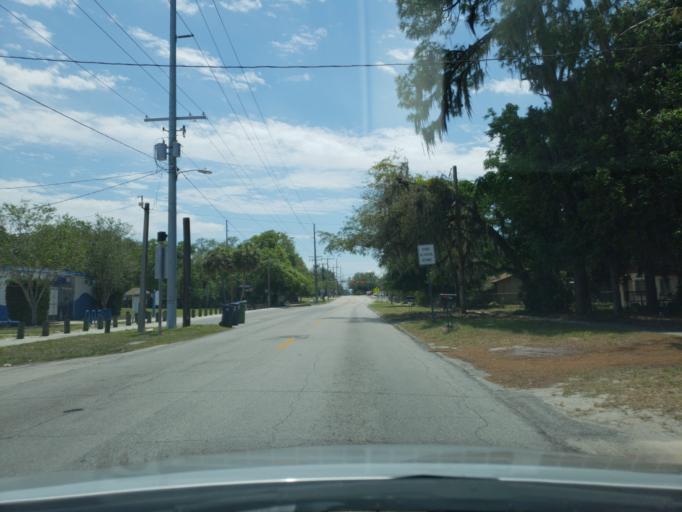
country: US
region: Florida
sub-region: Hillsborough County
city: Carrollwood
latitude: 28.0418
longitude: -82.4678
